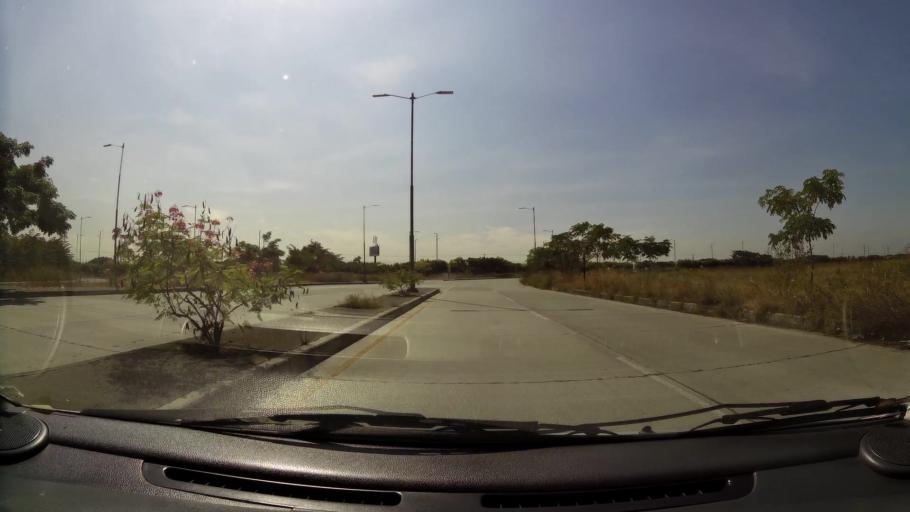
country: EC
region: Guayas
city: Eloy Alfaro
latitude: -2.0990
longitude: -79.8923
